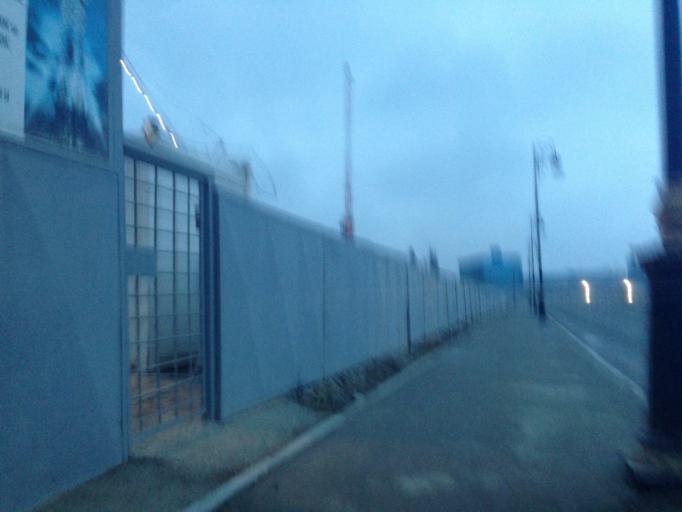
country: AZ
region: Baki
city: Baku
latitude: 40.4146
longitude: 49.8968
